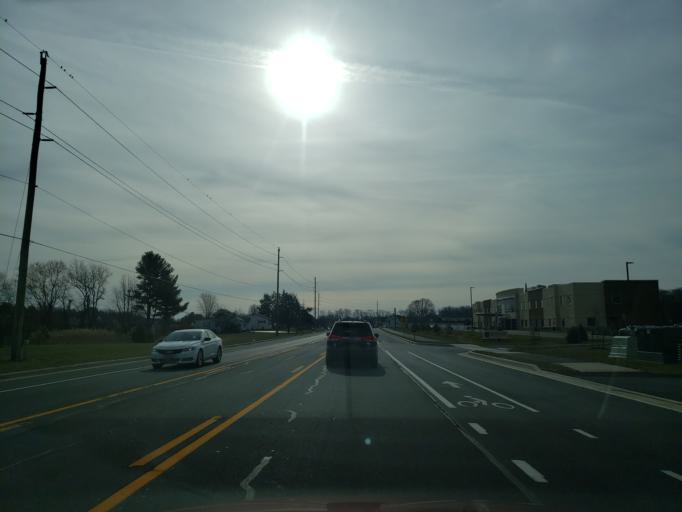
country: US
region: Delaware
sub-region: Kent County
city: Dover
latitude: 39.1785
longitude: -75.5561
